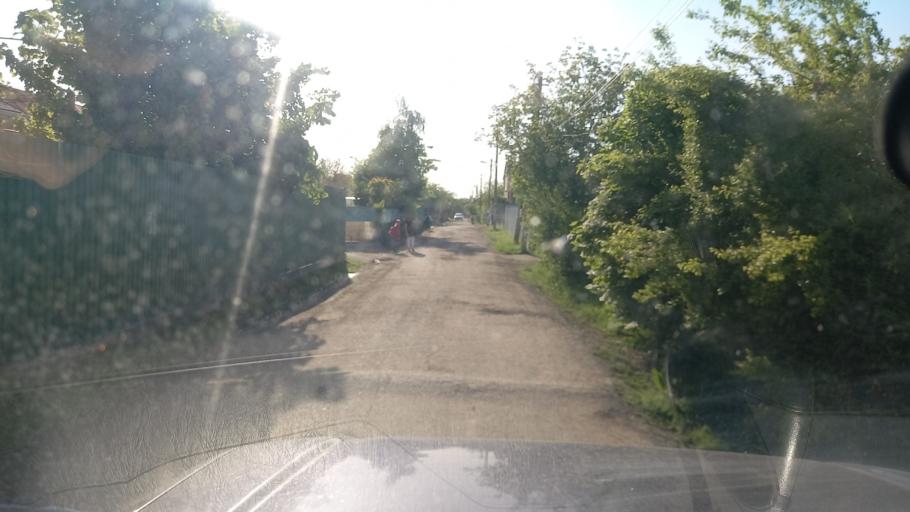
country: RU
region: Krasnodarskiy
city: Yelizavetinskaya
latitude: 45.0406
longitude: 38.7891
